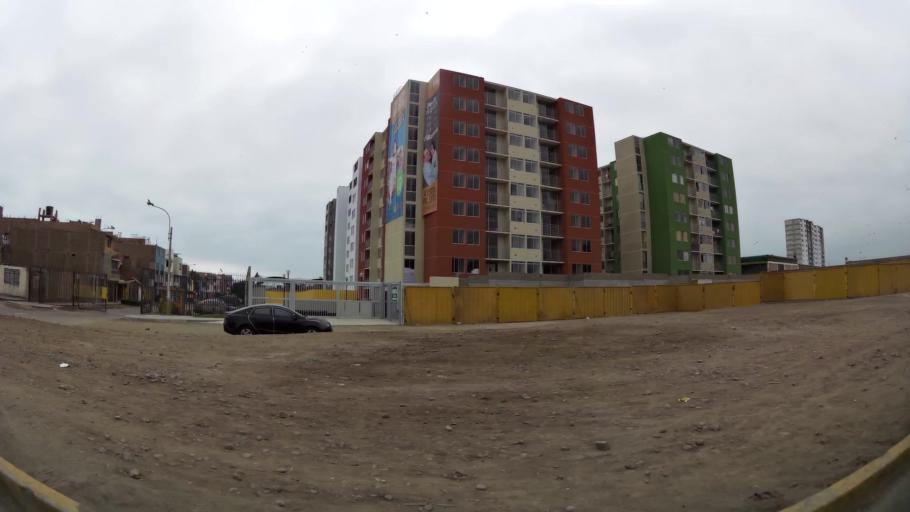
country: PE
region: Callao
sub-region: Callao
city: Callao
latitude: -12.0528
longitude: -77.1151
